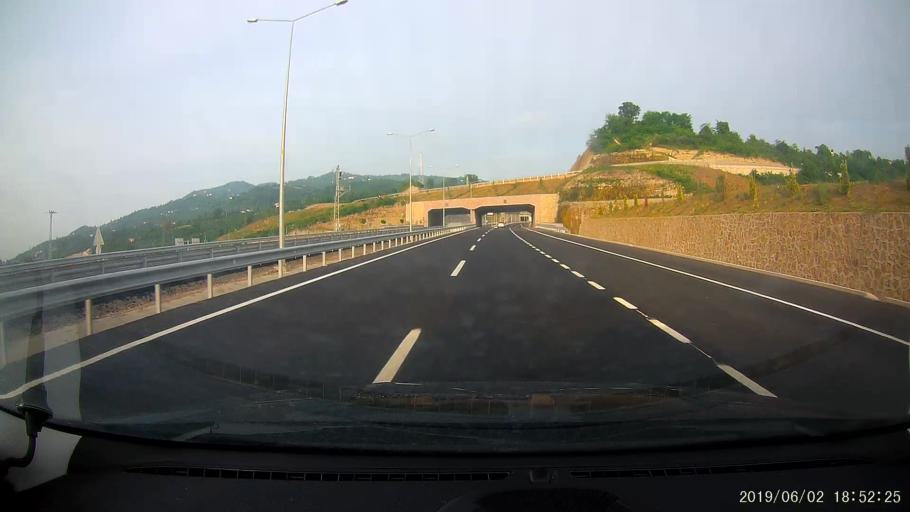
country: TR
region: Ordu
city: Ordu
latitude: 40.9888
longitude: 37.8108
